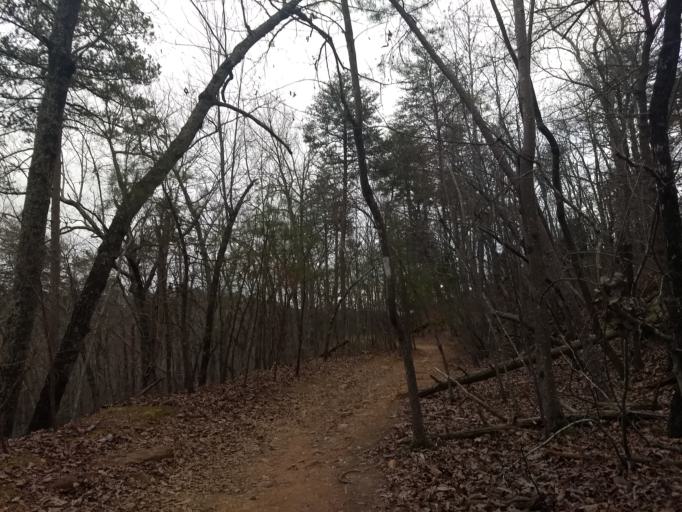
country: US
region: South Carolina
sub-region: Greenville County
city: Travelers Rest
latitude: 34.9434
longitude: -82.3966
